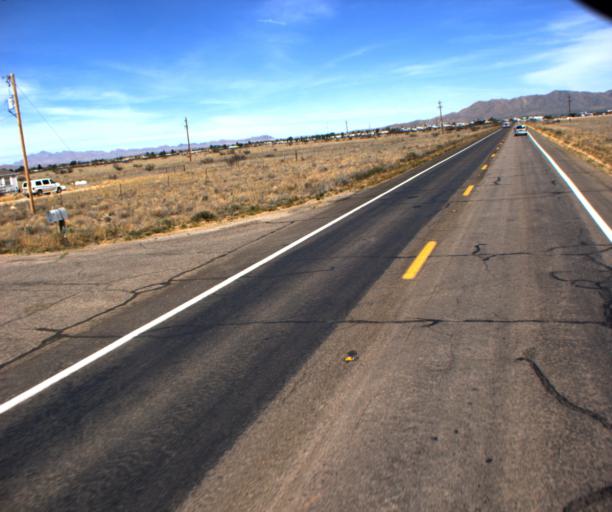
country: US
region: Arizona
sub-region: Cochise County
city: Willcox
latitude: 32.2370
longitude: -109.8481
